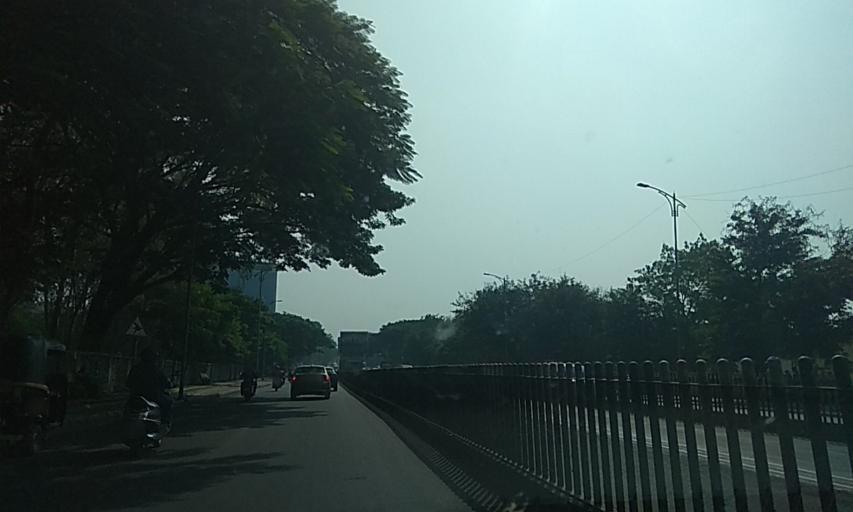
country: IN
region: Maharashtra
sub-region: Pune Division
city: Shivaji Nagar
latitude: 18.5462
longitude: 73.8751
